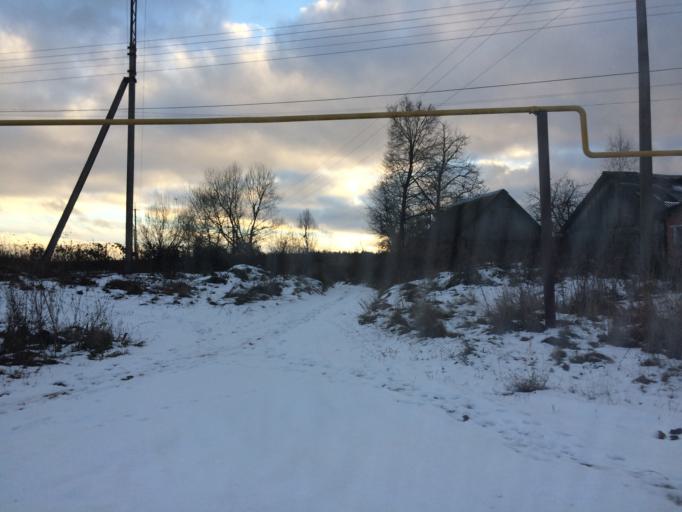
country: RU
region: Tula
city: Cherepet'
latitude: 54.1169
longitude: 36.3453
